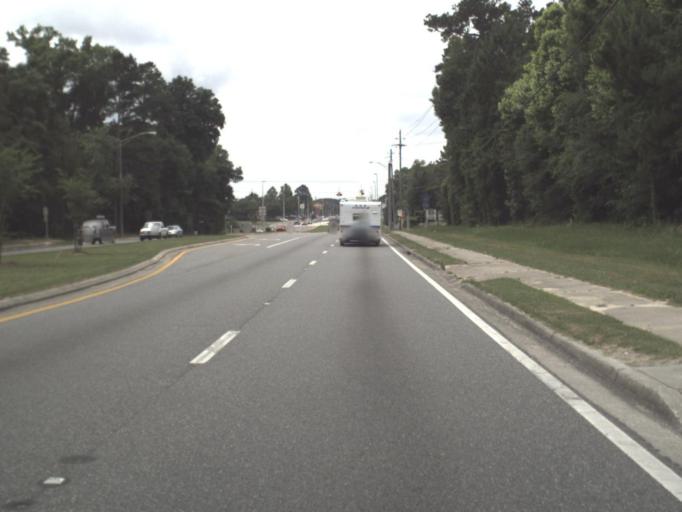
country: US
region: Florida
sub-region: Clay County
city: Middleburg
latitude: 30.0786
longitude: -81.8627
